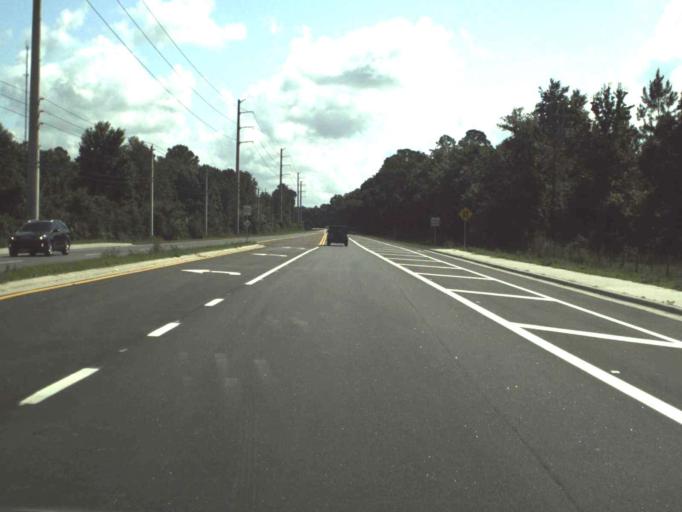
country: US
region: Florida
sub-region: Volusia County
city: Deltona
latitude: 28.8813
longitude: -81.1494
